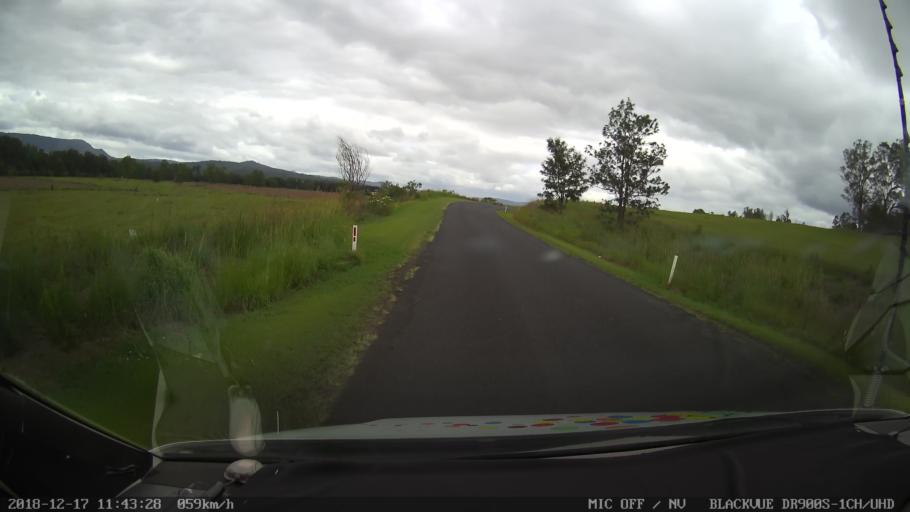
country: AU
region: New South Wales
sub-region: Kyogle
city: Kyogle
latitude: -28.6597
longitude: 152.5930
